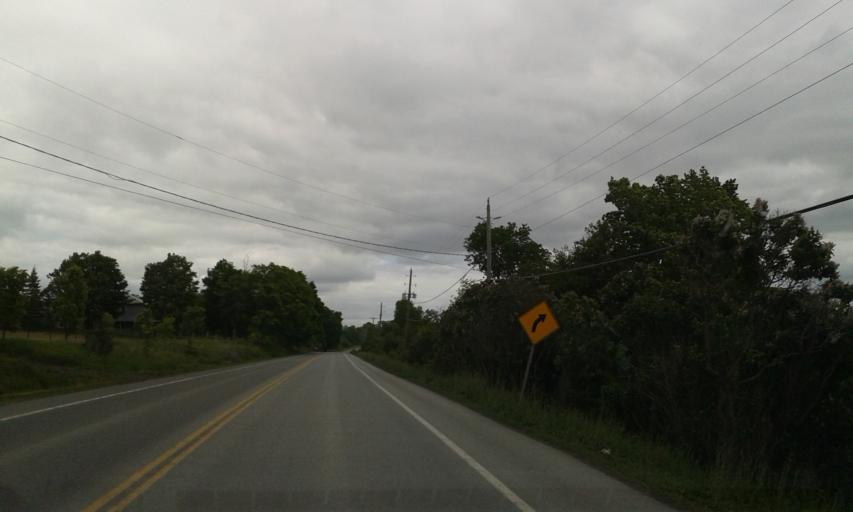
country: CA
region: Ontario
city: Skatepark
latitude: 44.1550
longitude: -76.8237
